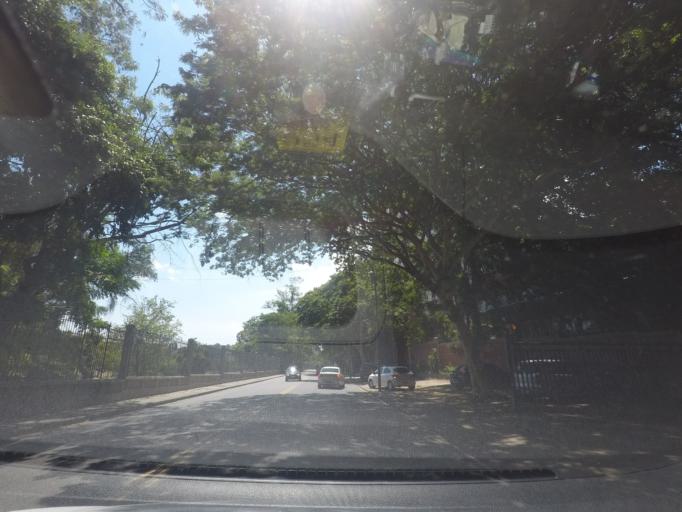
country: BR
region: Rio de Janeiro
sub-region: Rio De Janeiro
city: Rio de Janeiro
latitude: -22.9043
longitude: -43.2216
